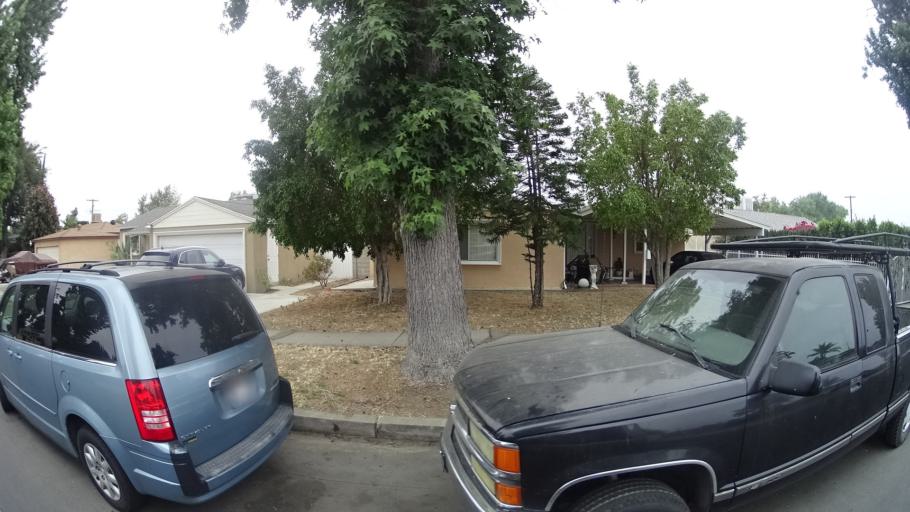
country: US
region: California
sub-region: Los Angeles County
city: Van Nuys
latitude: 34.1927
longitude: -118.4209
